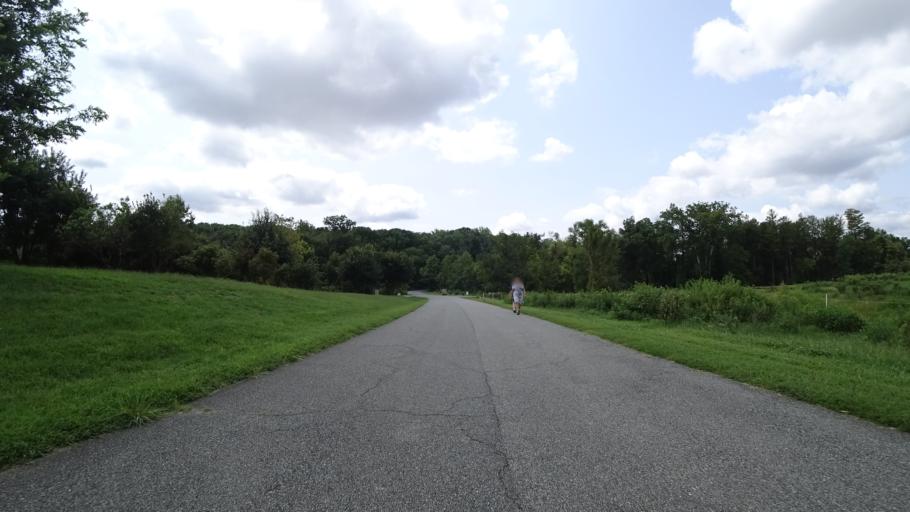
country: US
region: Maryland
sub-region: Prince George's County
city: Colmar Manor
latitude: 38.9135
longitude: -76.9641
